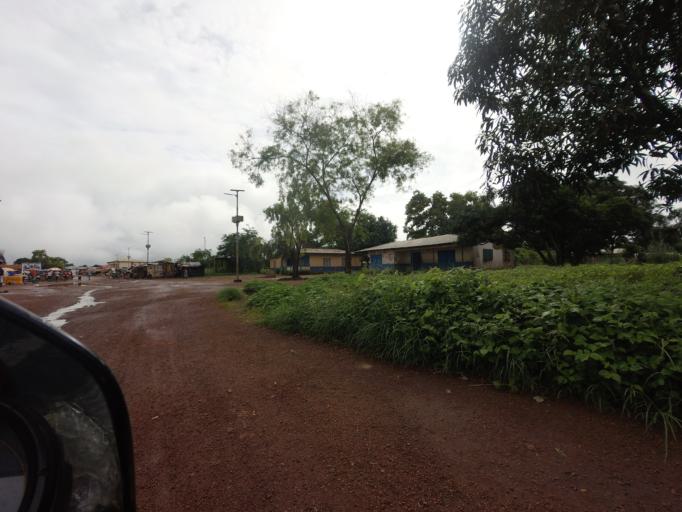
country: SL
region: Northern Province
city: Kambia
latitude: 9.1066
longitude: -12.9256
